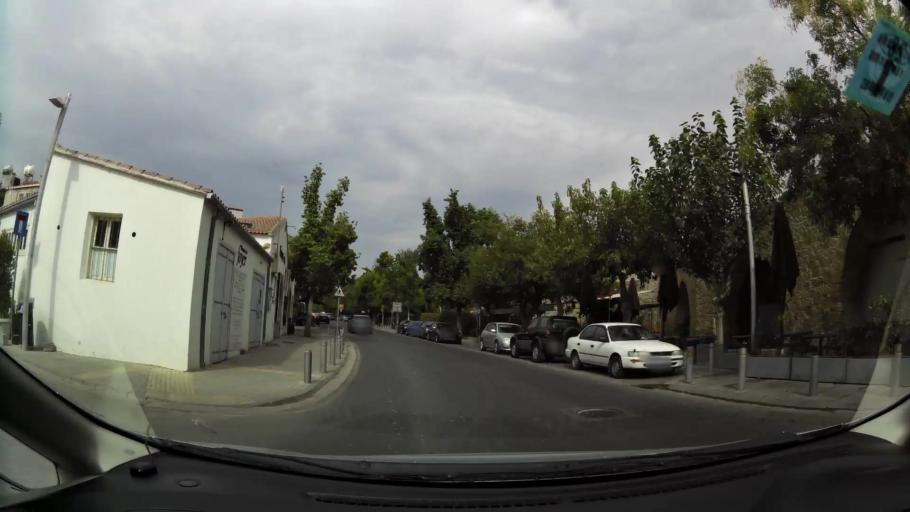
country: CY
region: Lefkosia
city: Nicosia
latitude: 35.1748
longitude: 33.3712
